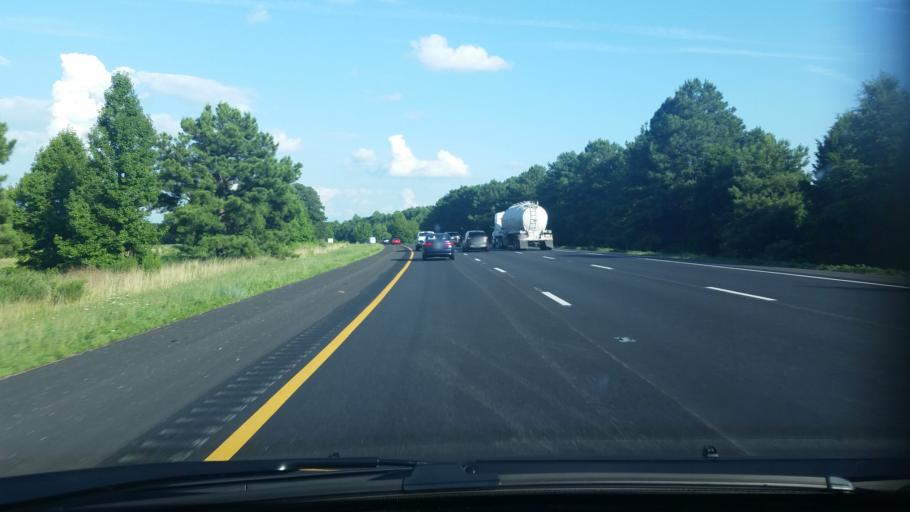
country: US
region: Virginia
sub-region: Henrico County
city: Chamberlayne
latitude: 37.6567
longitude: -77.4447
